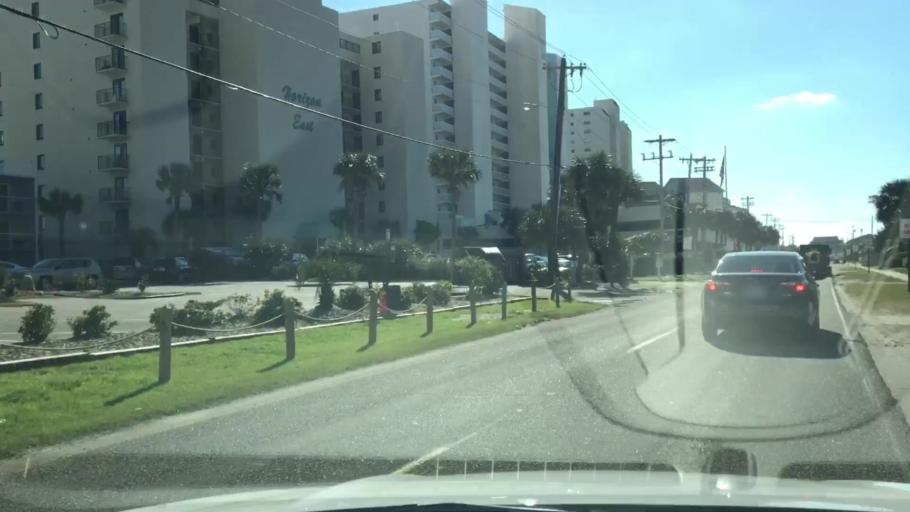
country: US
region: South Carolina
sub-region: Horry County
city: Garden City
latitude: 33.5855
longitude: -78.9911
